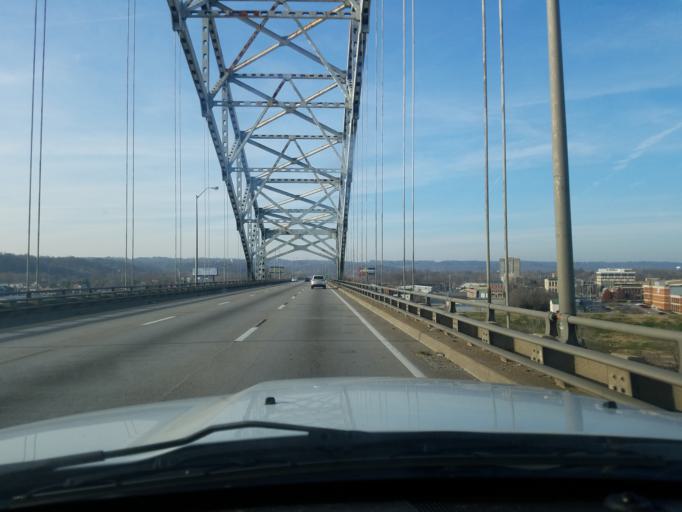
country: US
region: Indiana
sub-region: Floyd County
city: New Albany
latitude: 38.2795
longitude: -85.8230
